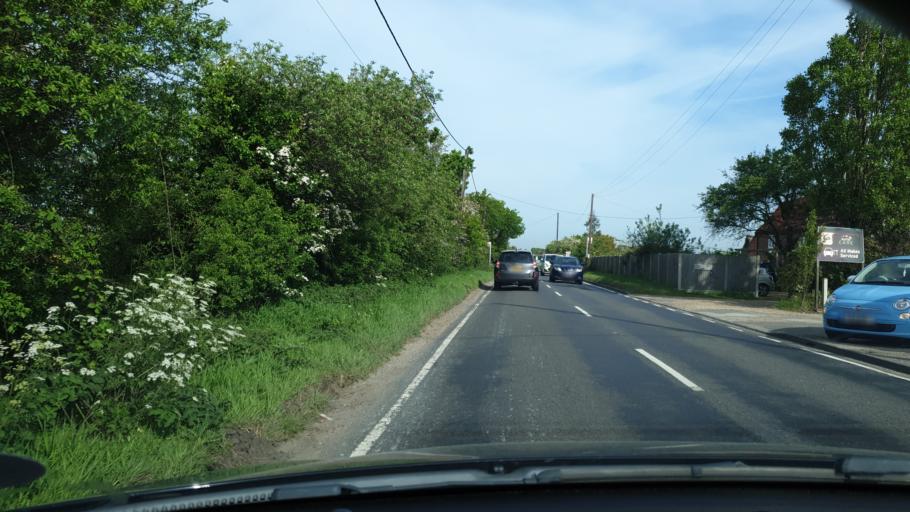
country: GB
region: England
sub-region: Essex
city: Little Clacton
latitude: 51.8515
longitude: 1.1868
